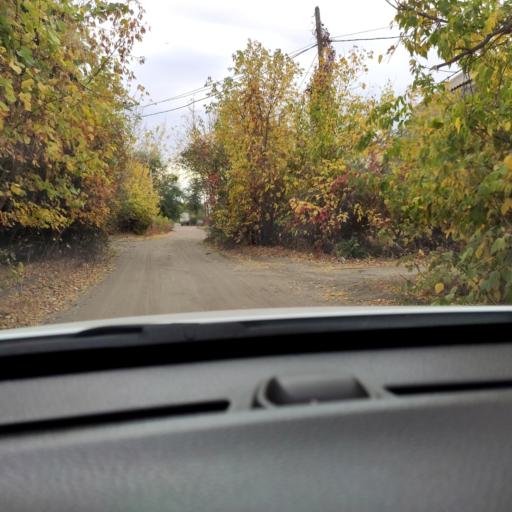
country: RU
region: Voronezj
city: Maslovka
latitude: 51.6061
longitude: 39.2788
